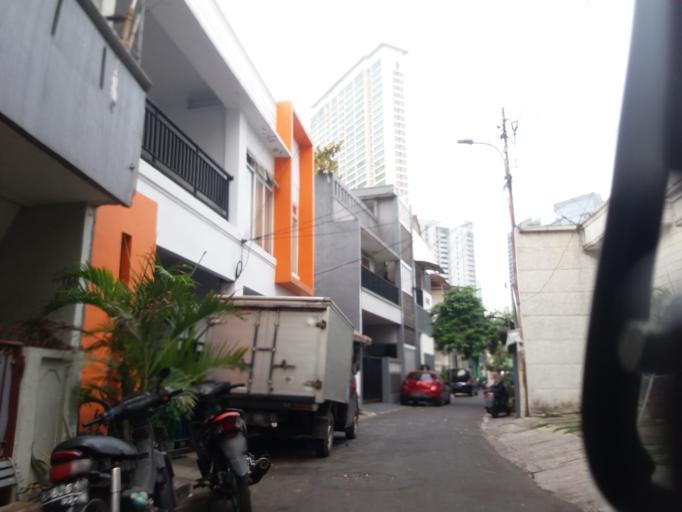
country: ID
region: Jakarta Raya
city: Jakarta
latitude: -6.2147
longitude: 106.8263
